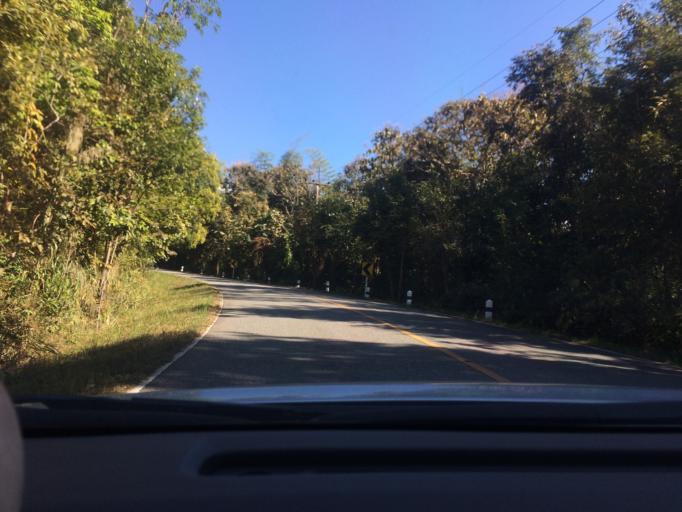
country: TH
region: Phitsanulok
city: Nakhon Thai
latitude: 17.0217
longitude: 100.9753
